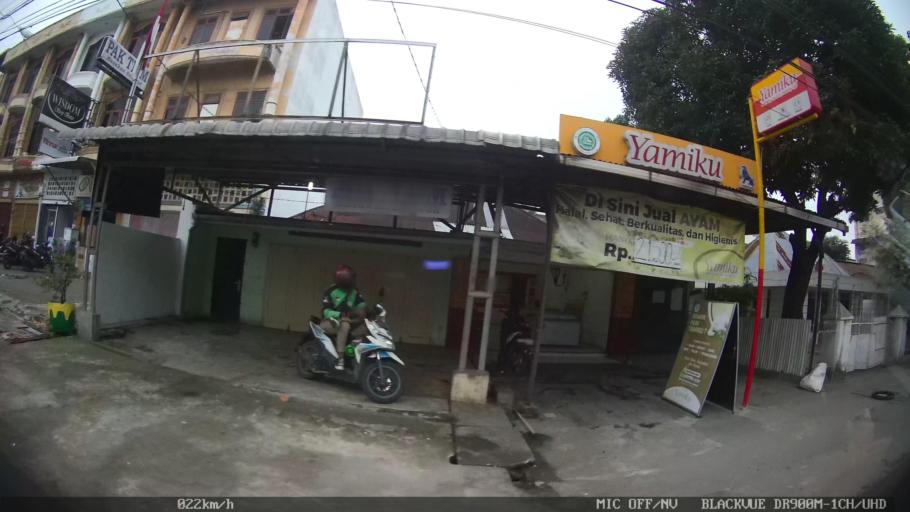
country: ID
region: North Sumatra
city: Medan
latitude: 3.5984
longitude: 98.7017
